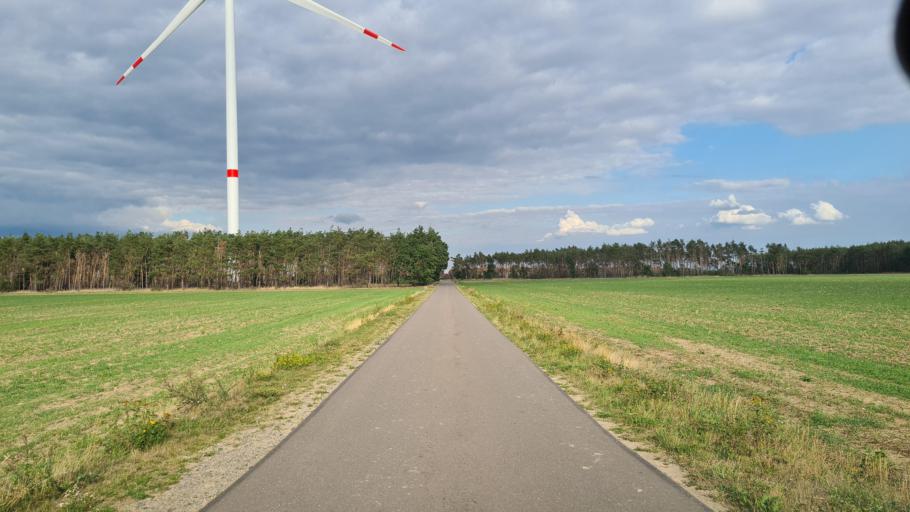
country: DE
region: Brandenburg
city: Falkenberg
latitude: 51.5669
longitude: 13.1968
